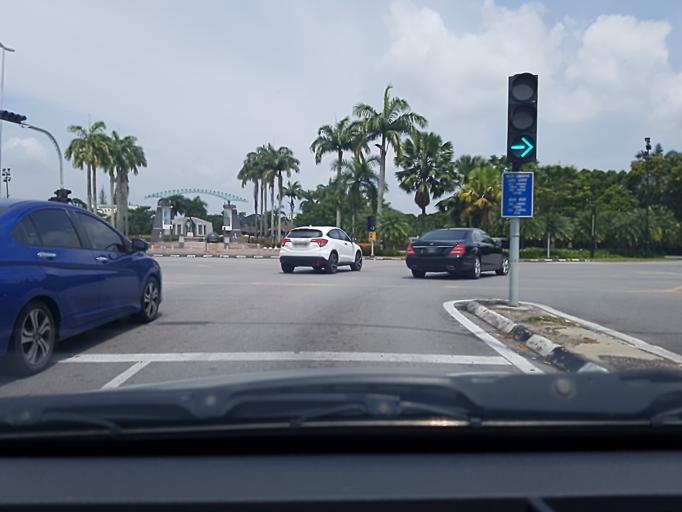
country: MY
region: Sarawak
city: Kuching
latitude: 1.5166
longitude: 110.3672
